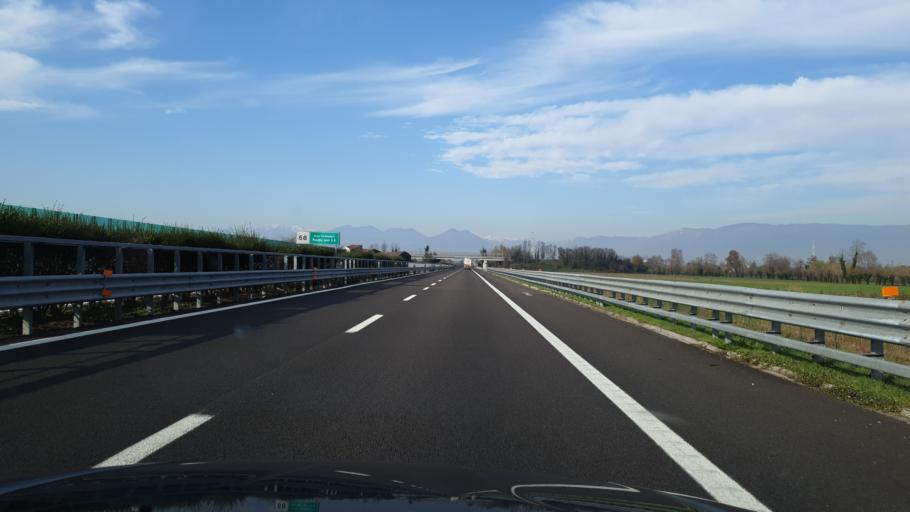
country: IT
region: Veneto
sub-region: Provincia di Vicenza
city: Vigardolo
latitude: 45.6319
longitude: 11.5842
